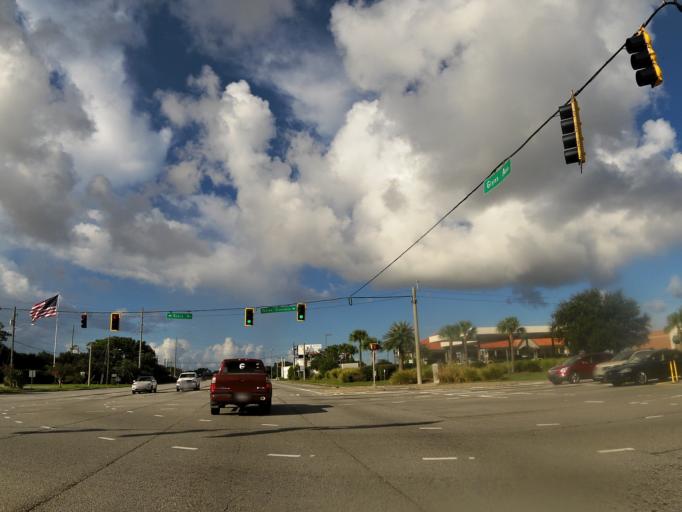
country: US
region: Georgia
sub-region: Glynn County
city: Brunswick
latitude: 31.1617
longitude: -81.4766
